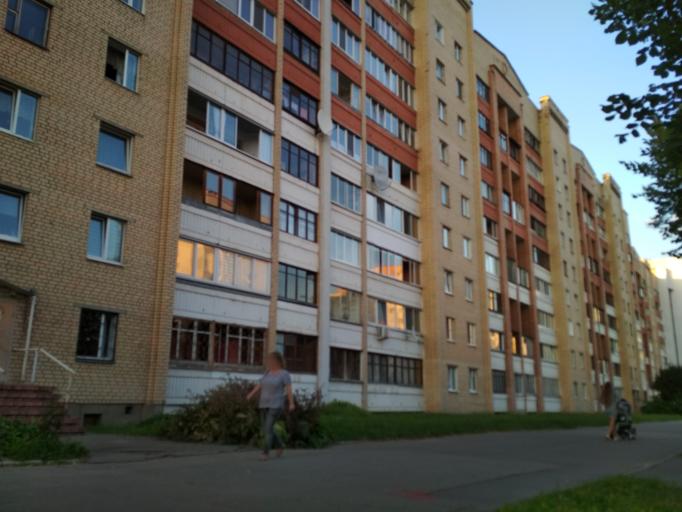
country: BY
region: Minsk
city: Minsk
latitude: 53.8784
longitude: 27.5400
